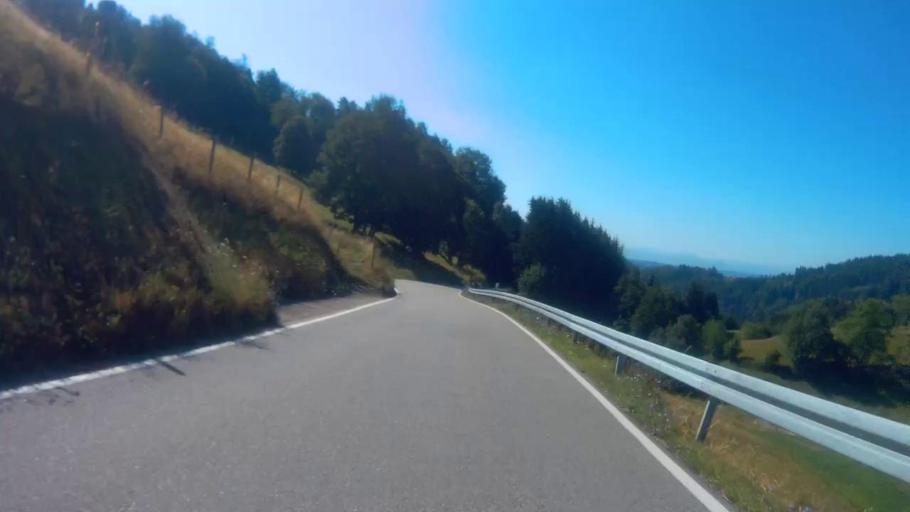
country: DE
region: Baden-Wuerttemberg
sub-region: Freiburg Region
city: Zell im Wiesental
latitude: 47.7156
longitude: 7.8402
